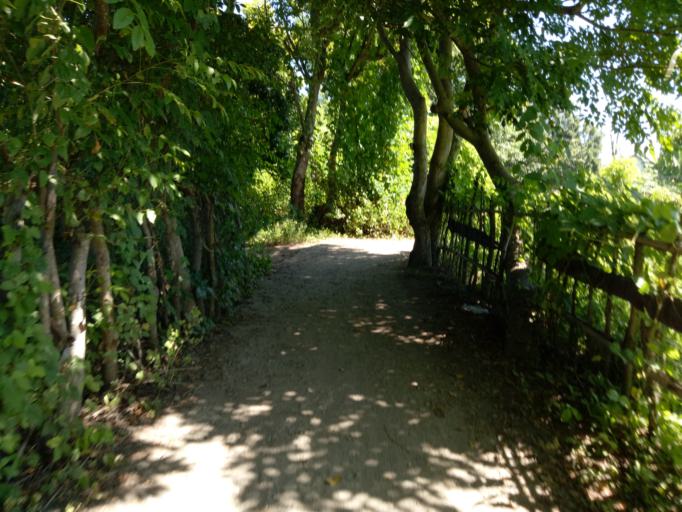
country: ID
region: West Nusa Tenggara
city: Gili Air
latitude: -8.3555
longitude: 116.0816
